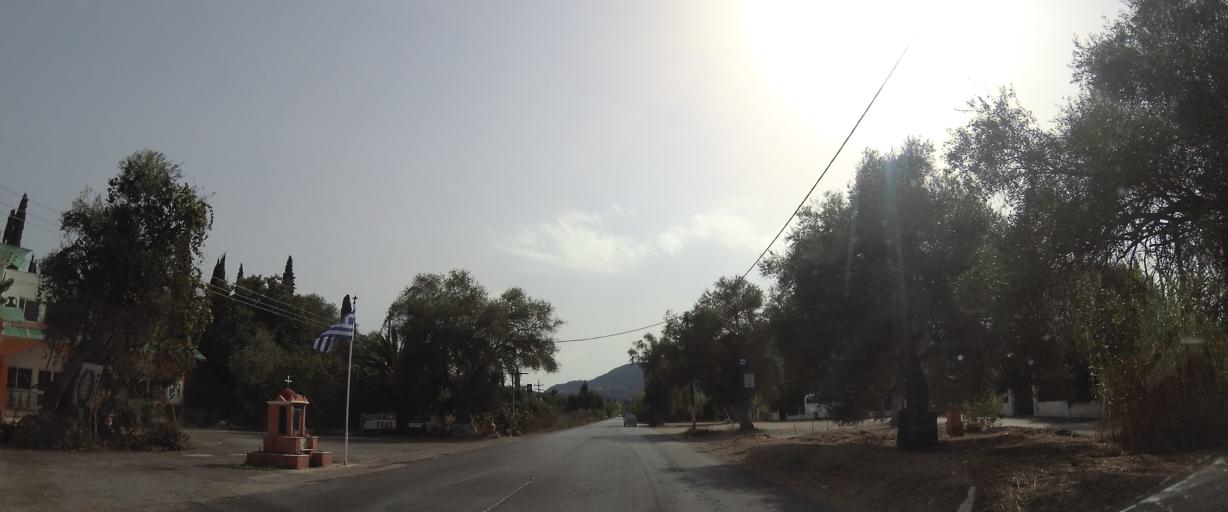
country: GR
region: Ionian Islands
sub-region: Nomos Kerkyras
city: Kynopiastes
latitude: 39.5758
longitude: 19.8930
